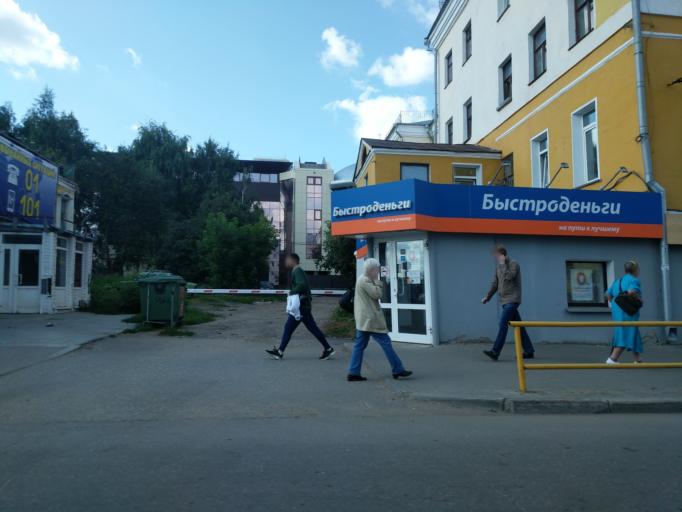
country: RU
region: Kirov
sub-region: Kirovo-Chepetskiy Rayon
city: Kirov
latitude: 58.6053
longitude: 49.6807
